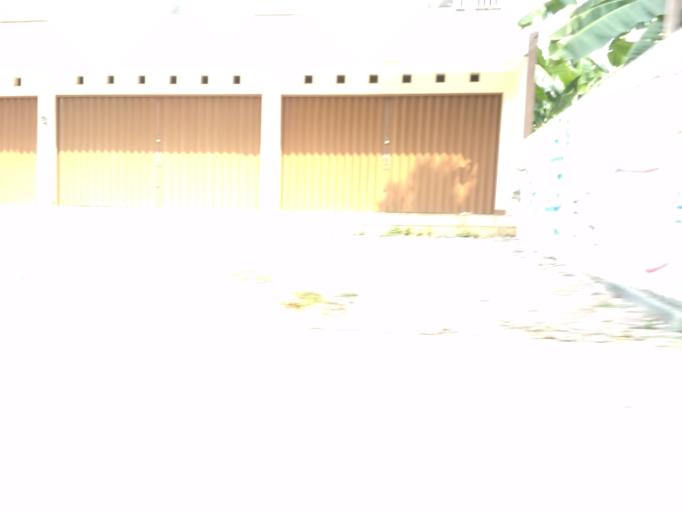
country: ID
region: West Java
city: Bogor
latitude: -6.5709
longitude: 106.7529
